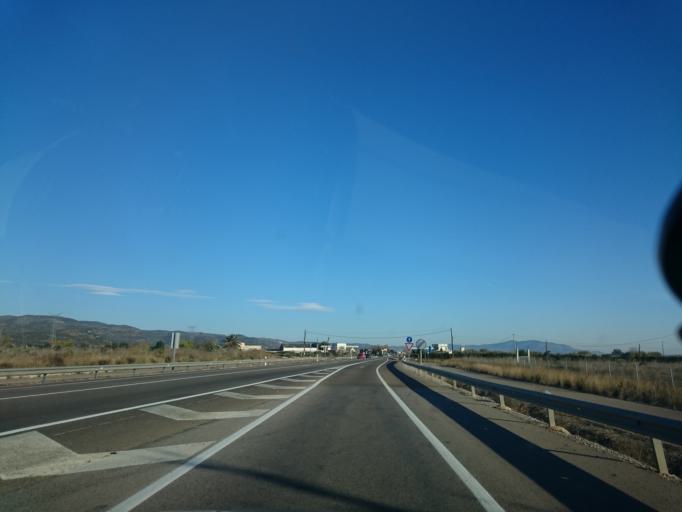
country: ES
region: Valencia
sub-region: Provincia de Castello
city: Orpesa/Oropesa del Mar
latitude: 40.1322
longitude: 0.1482
